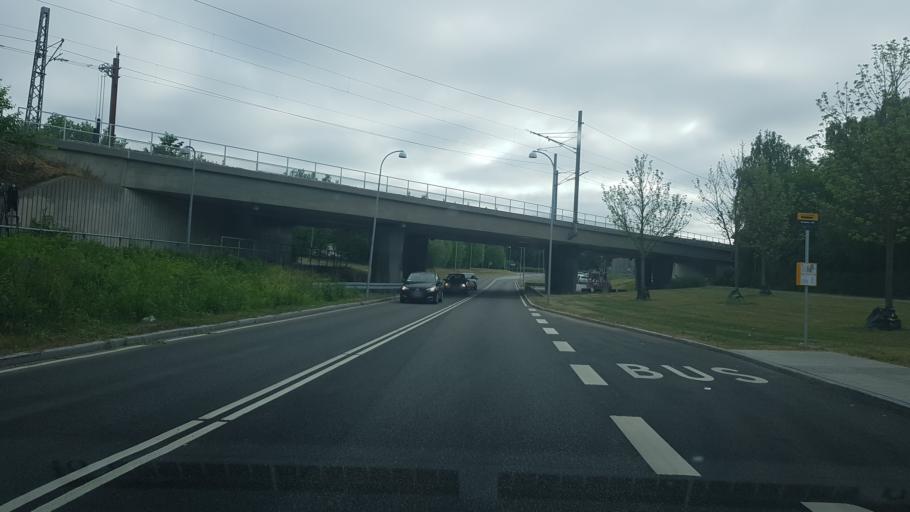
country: DK
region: Capital Region
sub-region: Vallensbaek Kommune
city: Vallensbaek
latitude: 55.6233
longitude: 12.3941
